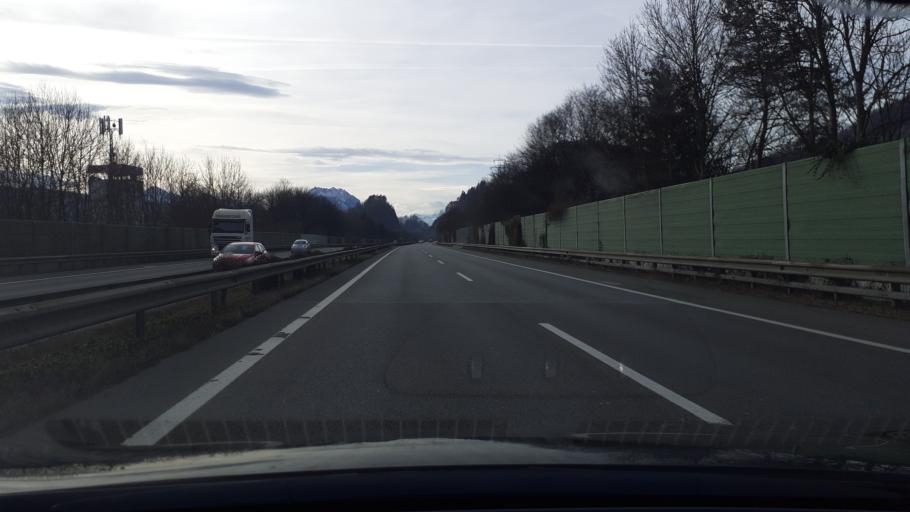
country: AT
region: Vorarlberg
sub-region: Politischer Bezirk Feldkirch
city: Gotzis
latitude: 47.3420
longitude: 9.6336
